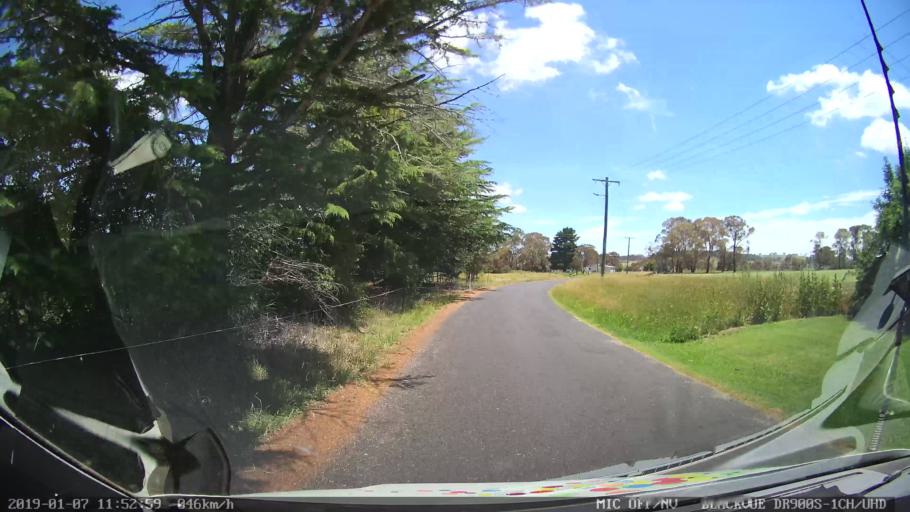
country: AU
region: New South Wales
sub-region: Guyra
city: Guyra
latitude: -30.3078
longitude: 151.6563
